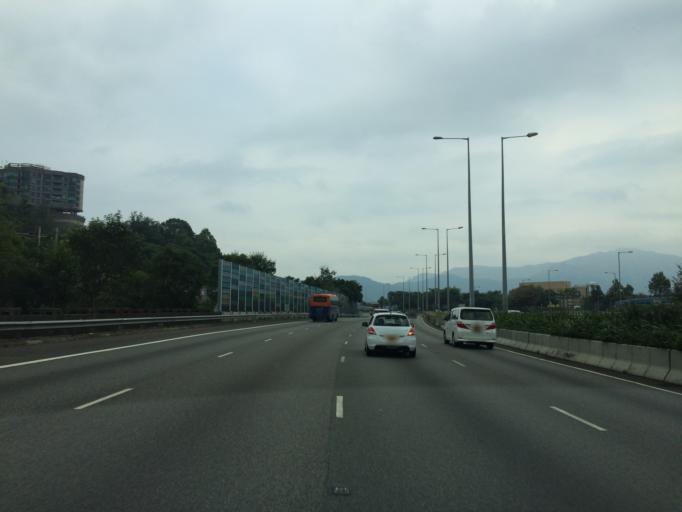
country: HK
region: Tai Po
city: Tai Po
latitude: 22.4319
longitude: 114.2008
